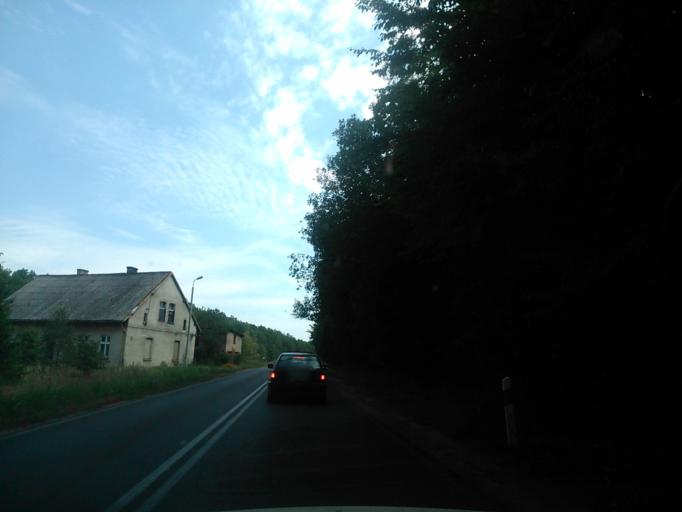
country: PL
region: Warmian-Masurian Voivodeship
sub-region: Powiat dzialdowski
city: Ilowo -Osada
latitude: 53.1583
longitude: 20.3092
